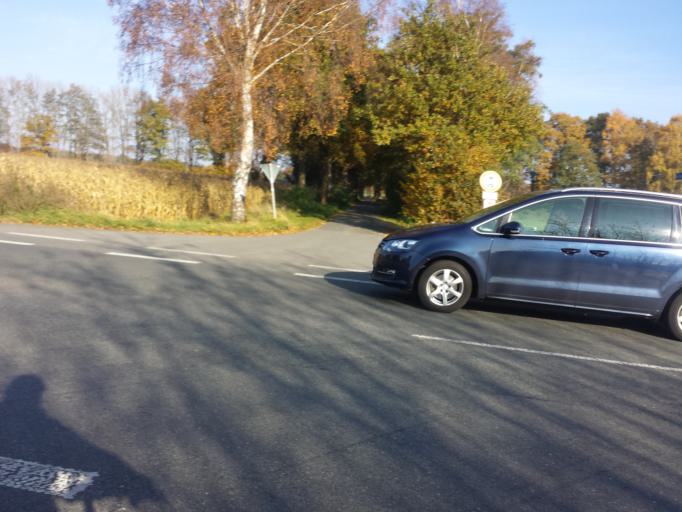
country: DE
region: North Rhine-Westphalia
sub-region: Regierungsbezirk Detmold
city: Guetersloh
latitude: 51.9230
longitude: 8.3317
